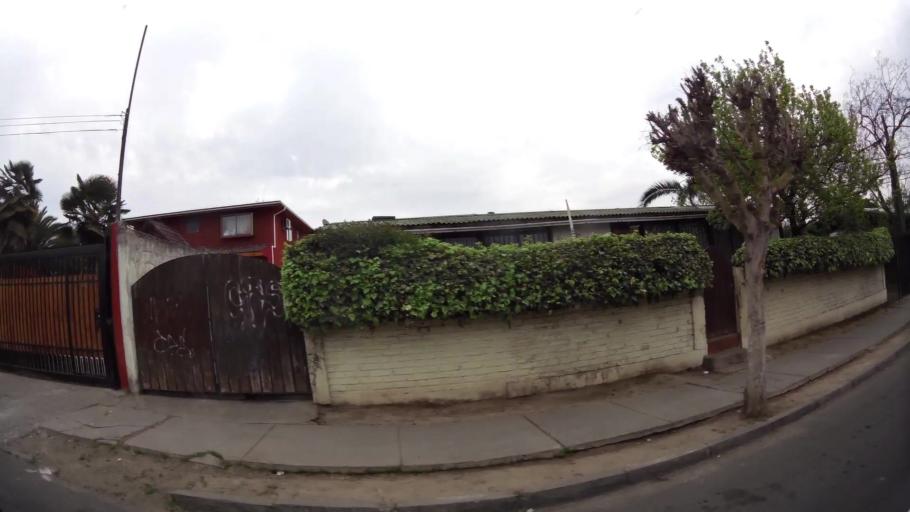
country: CL
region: Santiago Metropolitan
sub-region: Provincia de Santiago
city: Lo Prado
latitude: -33.5047
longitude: -70.7619
